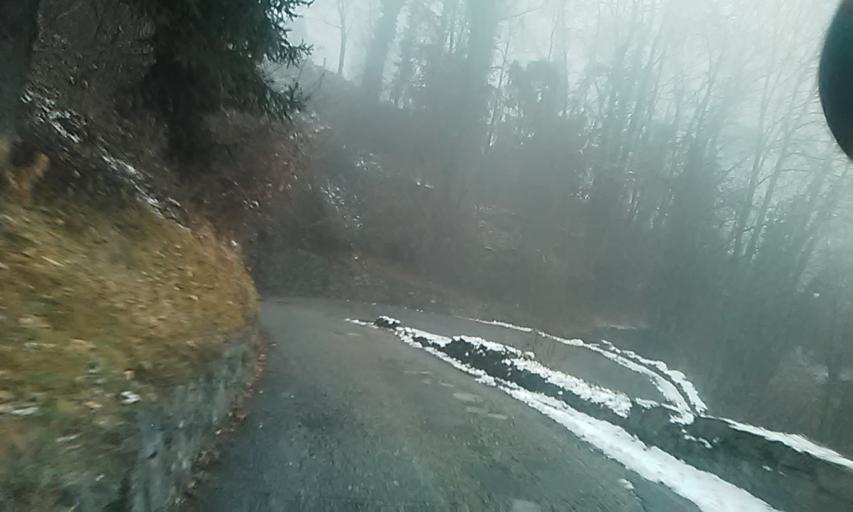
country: IT
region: Piedmont
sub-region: Provincia di Vercelli
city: Varallo
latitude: 45.8401
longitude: 8.2637
